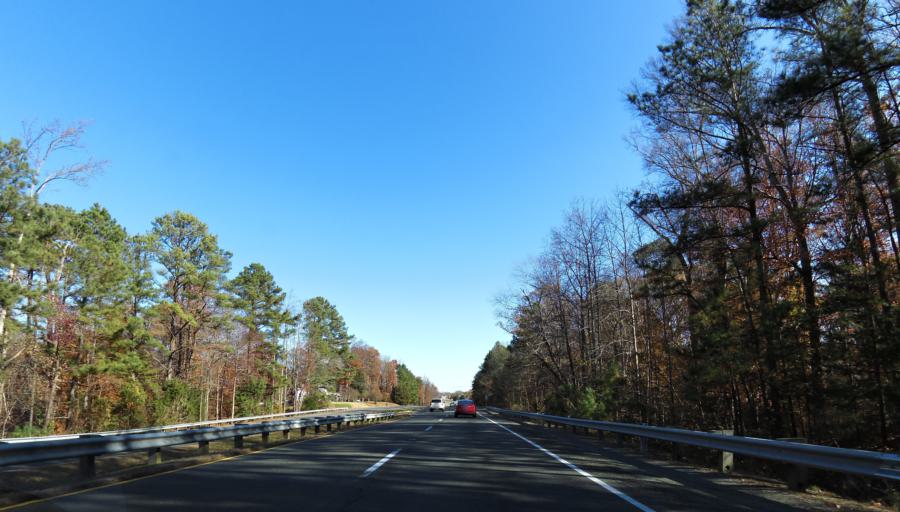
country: US
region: Virginia
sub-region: Henrico County
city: Chamberlayne
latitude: 37.6537
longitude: -77.3936
